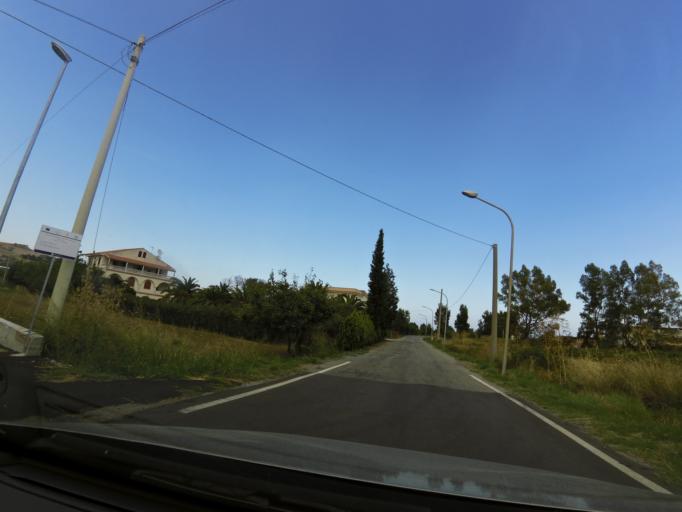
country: IT
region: Calabria
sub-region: Provincia di Reggio Calabria
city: Monasterace Marina
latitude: 38.4229
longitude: 16.5462
